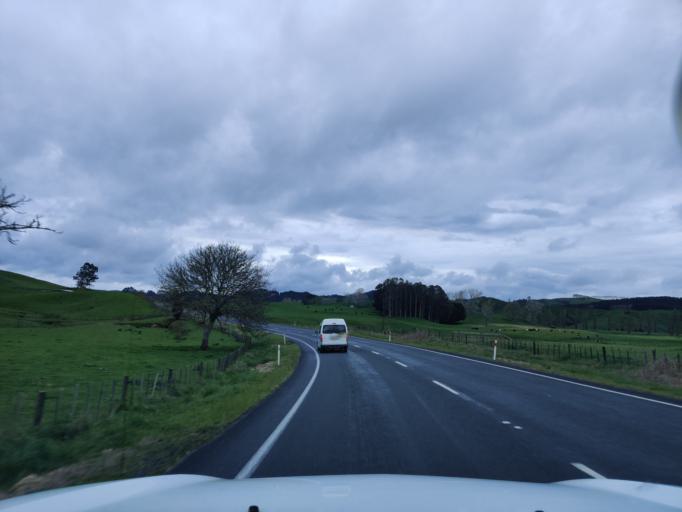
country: NZ
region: Waikato
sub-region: Otorohanga District
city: Otorohanga
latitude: -38.4570
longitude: 175.1676
